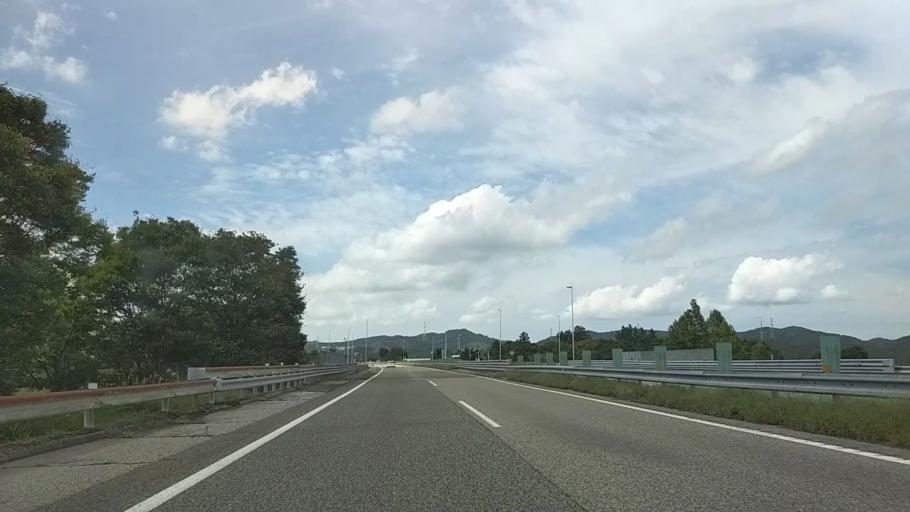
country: JP
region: Toyama
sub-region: Oyabe Shi
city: Oyabe
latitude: 36.6300
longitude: 136.8513
